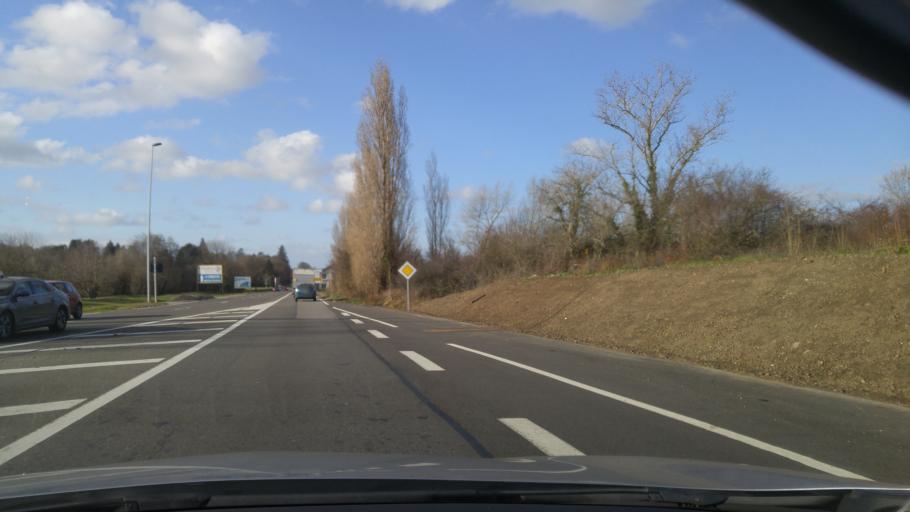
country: FR
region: Rhone-Alpes
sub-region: Departement de l'Isere
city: Villefontaine
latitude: 45.6273
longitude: 5.1625
